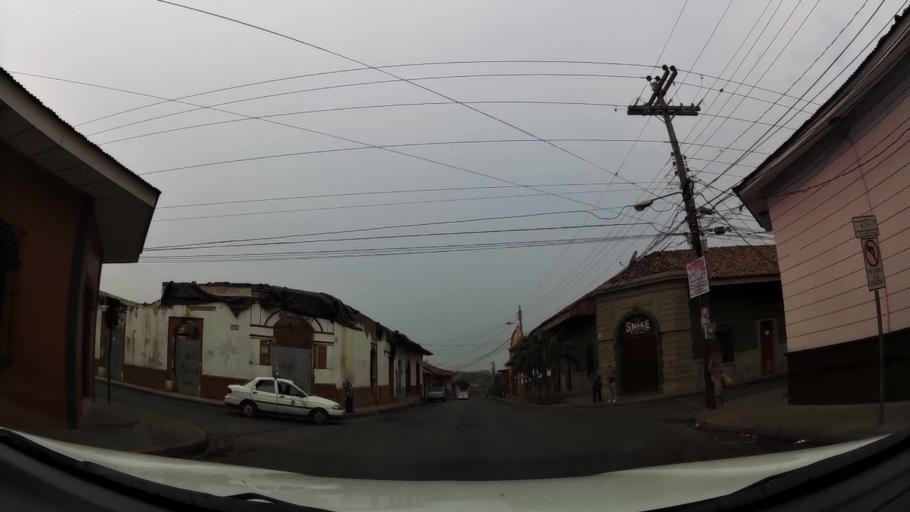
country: NI
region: Leon
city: Leon
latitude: 12.4344
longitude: -86.8805
